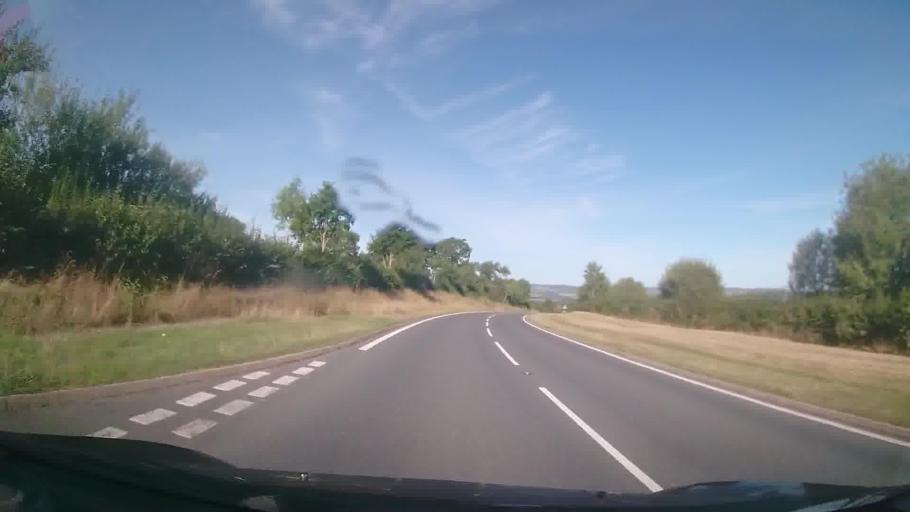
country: GB
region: Wales
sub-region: Sir Powys
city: Hay
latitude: 51.9818
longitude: -3.2295
